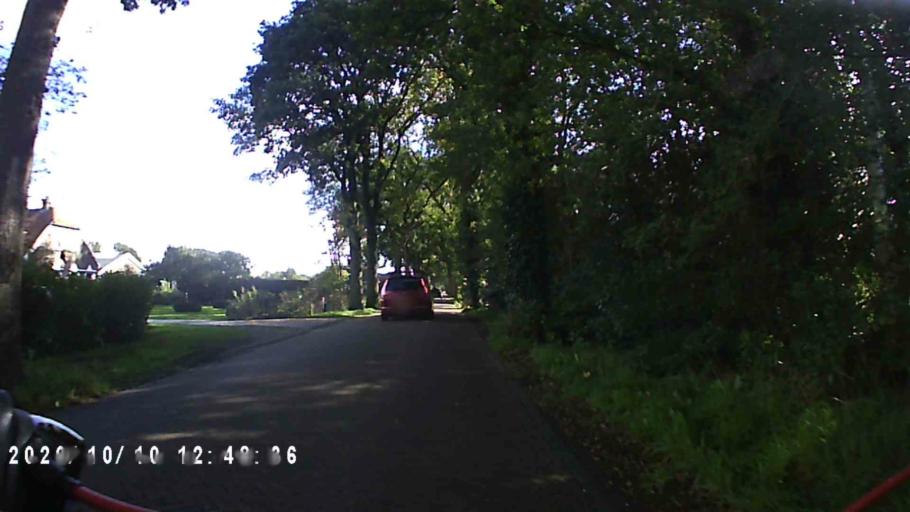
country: NL
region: Friesland
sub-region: Gemeente Weststellingwerf
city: Noordwolde
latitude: 52.9224
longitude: 6.2436
